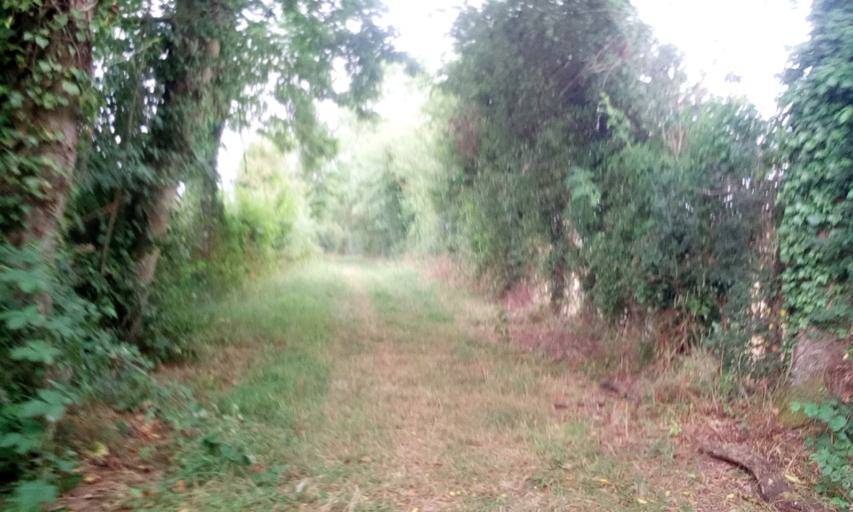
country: FR
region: Lower Normandy
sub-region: Departement du Calvados
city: Thury-Harcourt
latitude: 48.9871
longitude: -0.4187
